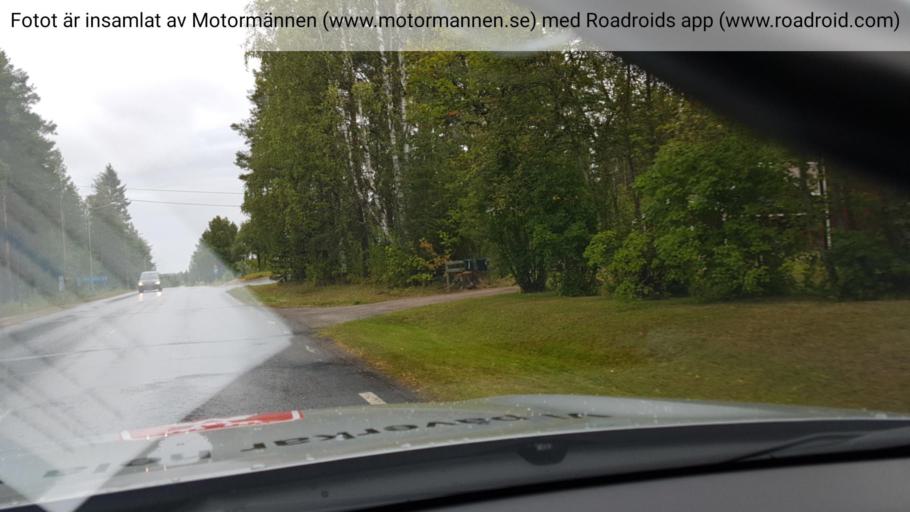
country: SE
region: Norrbotten
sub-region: Alvsbyns Kommun
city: AElvsbyn
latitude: 66.0941
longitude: 20.9446
